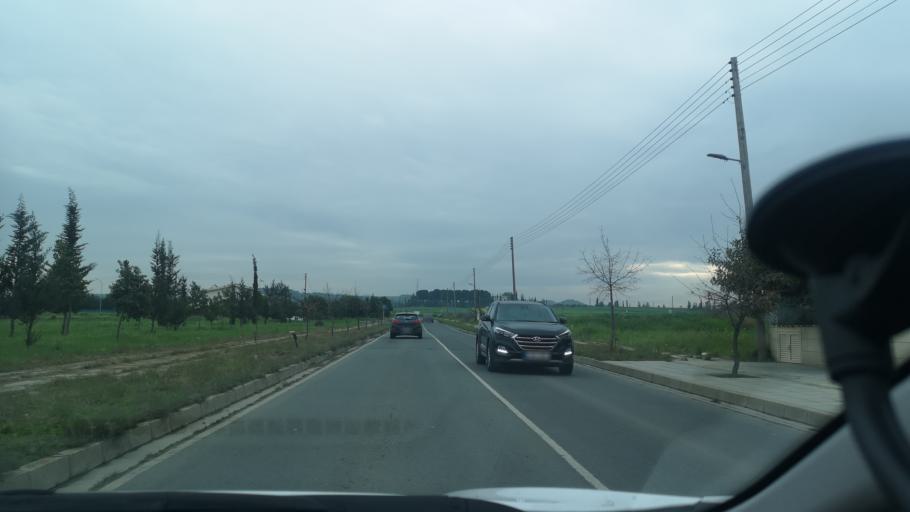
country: CY
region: Lefkosia
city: Tseri
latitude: 35.1041
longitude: 33.3493
